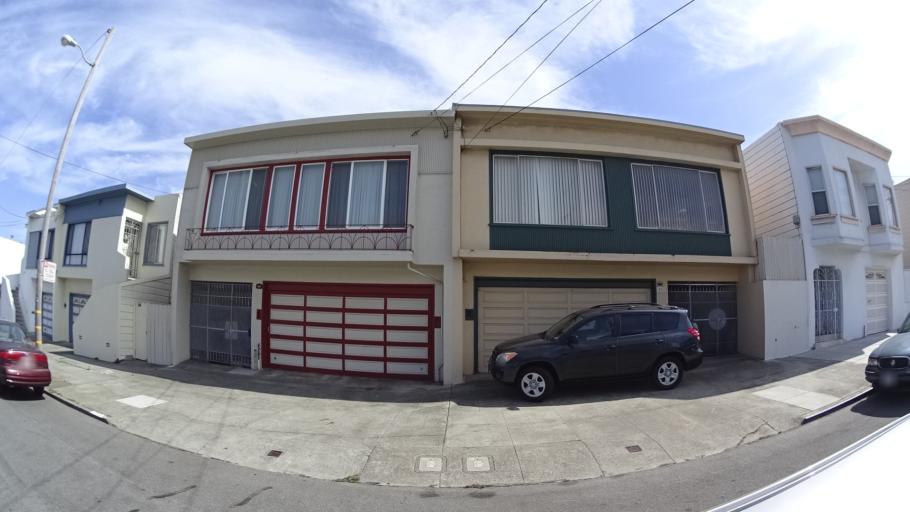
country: US
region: California
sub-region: San Mateo County
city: Daly City
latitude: 37.7124
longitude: -122.4465
